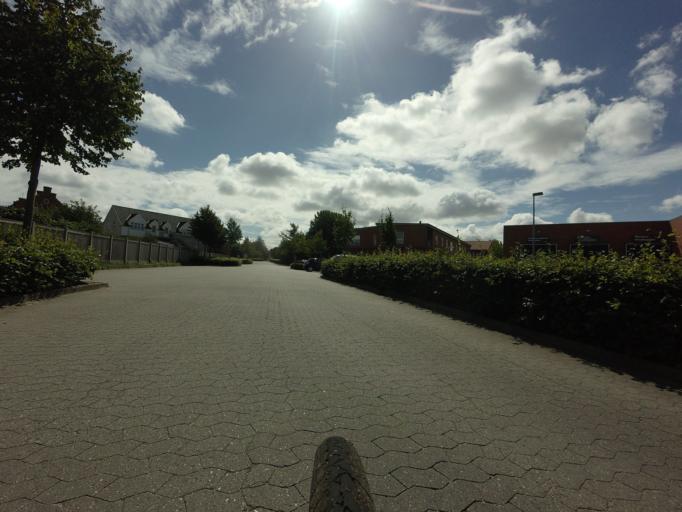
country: DK
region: Central Jutland
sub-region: Norddjurs Kommune
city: Auning
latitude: 56.4323
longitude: 10.3752
